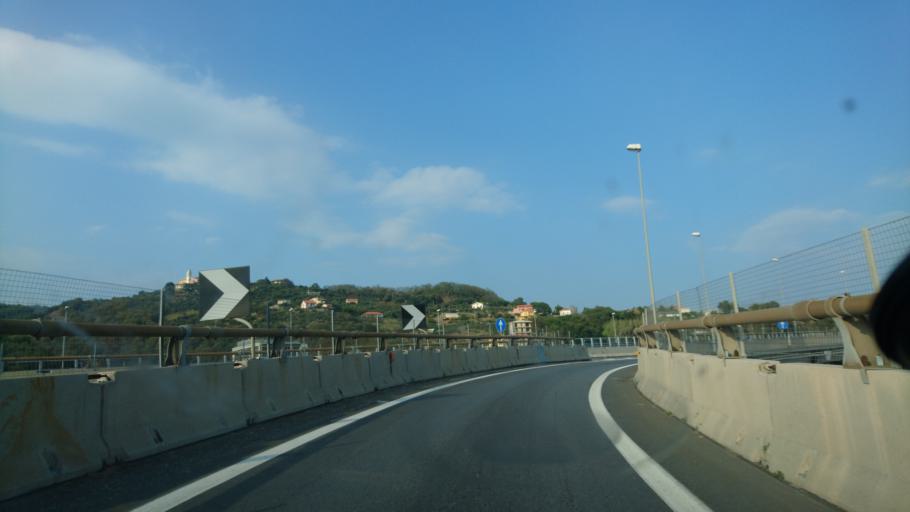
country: IT
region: Liguria
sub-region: Provincia di Savona
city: Valleggia
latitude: 44.2875
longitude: 8.4398
